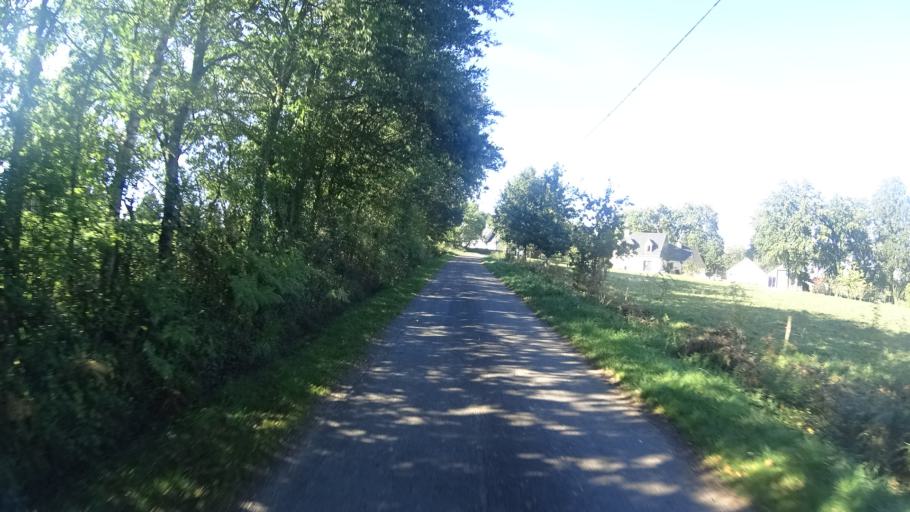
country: FR
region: Brittany
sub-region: Departement du Morbihan
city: Peillac
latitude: 47.7108
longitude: -2.2110
